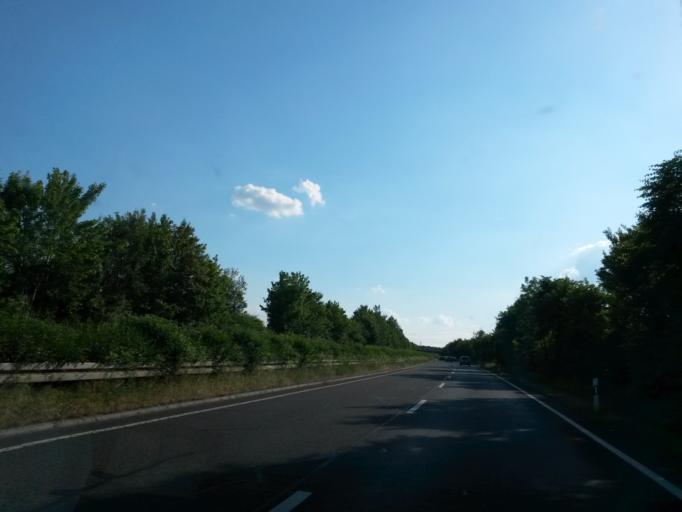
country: DE
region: Bavaria
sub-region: Regierungsbezirk Mittelfranken
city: Puschendorf
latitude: 49.4887
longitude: 10.8358
